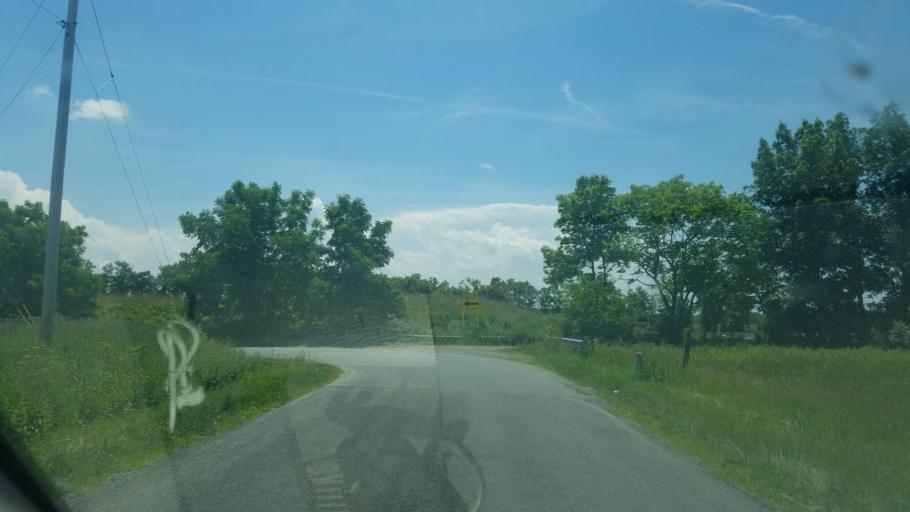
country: US
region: Ohio
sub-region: Hancock County
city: Findlay
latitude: 40.9938
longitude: -83.6362
